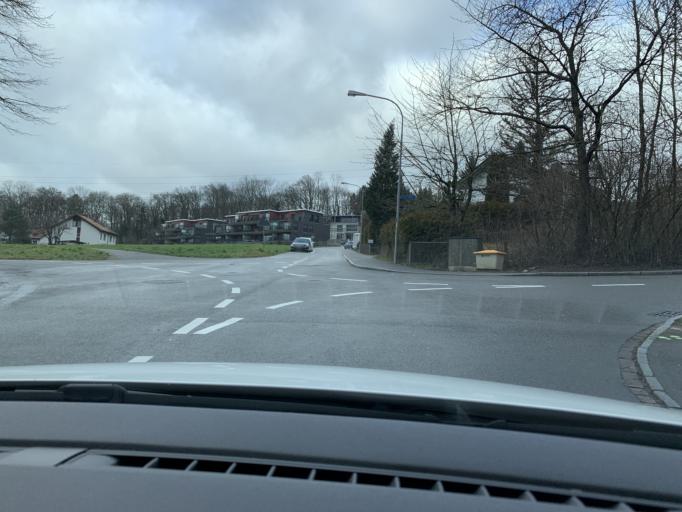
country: CH
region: Zurich
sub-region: Bezirk Dielsdorf
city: Sonnhalde
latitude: 47.4541
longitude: 8.4605
